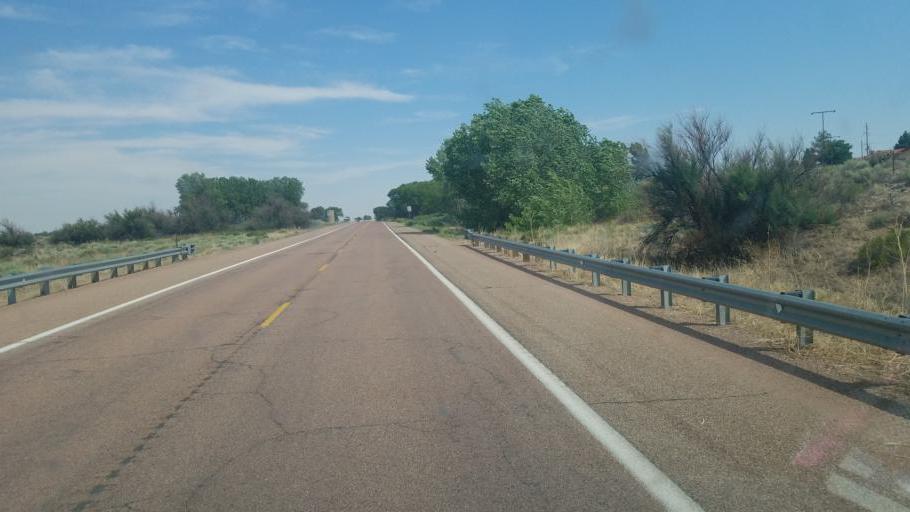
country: US
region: Colorado
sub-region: Pueblo County
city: Pueblo
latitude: 38.2389
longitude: -104.3347
